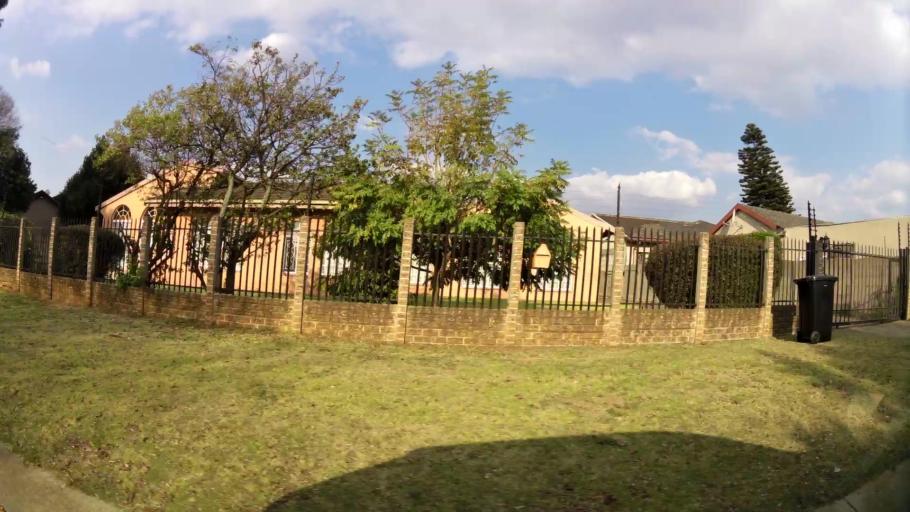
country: ZA
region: Gauteng
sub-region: City of Johannesburg Metropolitan Municipality
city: Modderfontein
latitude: -26.1164
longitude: 28.2048
